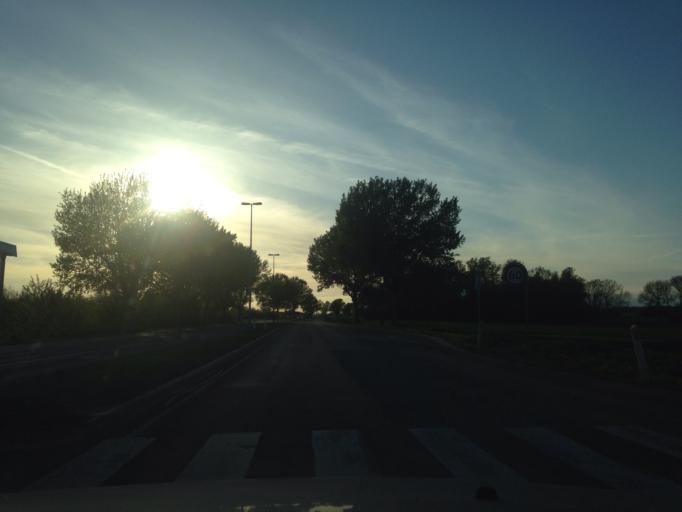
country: DK
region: Zealand
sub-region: Greve Kommune
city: Greve
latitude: 55.5897
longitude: 12.2467
